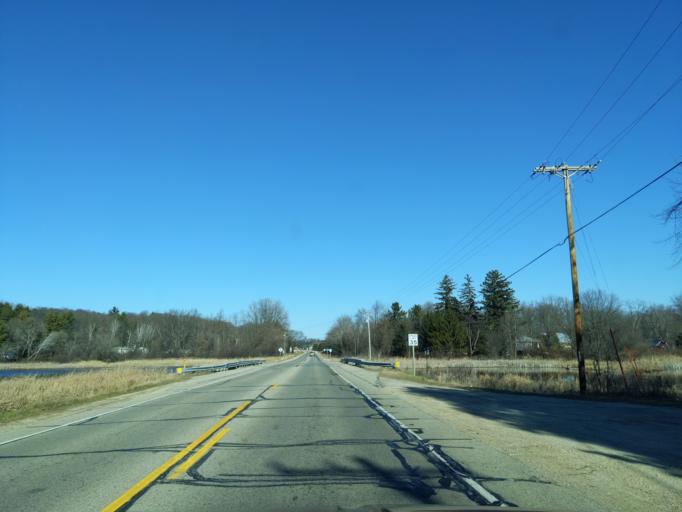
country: US
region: Wisconsin
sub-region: Waushara County
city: Wautoma
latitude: 44.0773
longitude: -89.2928
